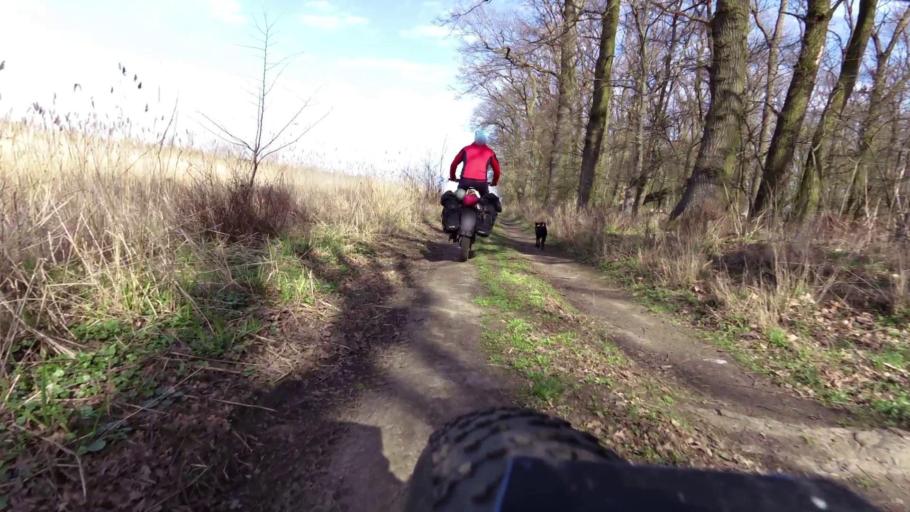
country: PL
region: Lubusz
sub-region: Powiat slubicki
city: Slubice
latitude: 52.3321
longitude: 14.5646
